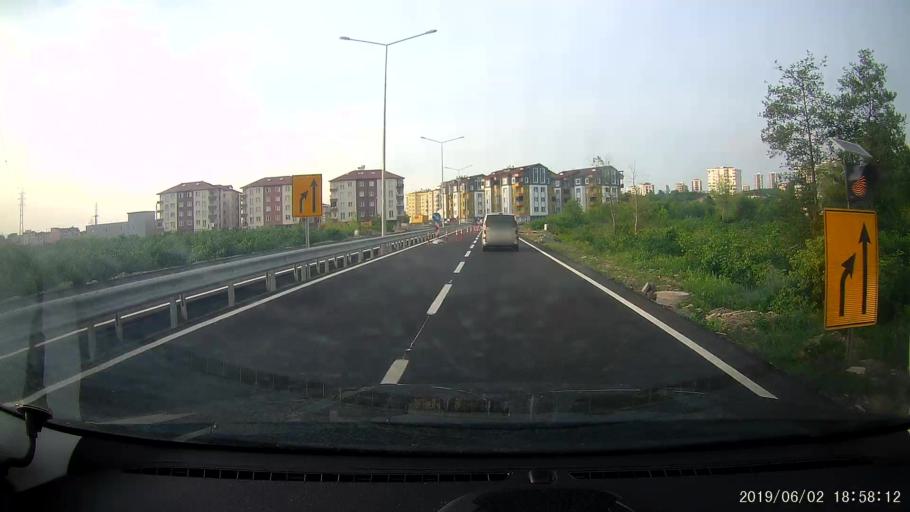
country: TR
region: Ordu
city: Ordu
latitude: 40.9598
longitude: 37.9067
